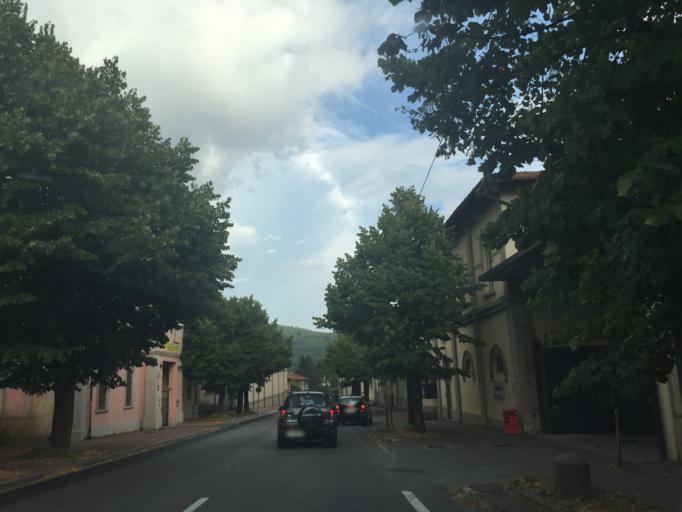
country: IT
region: Tuscany
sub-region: Provincia di Pistoia
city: Campo Tizzoro
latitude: 44.0385
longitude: 10.8647
